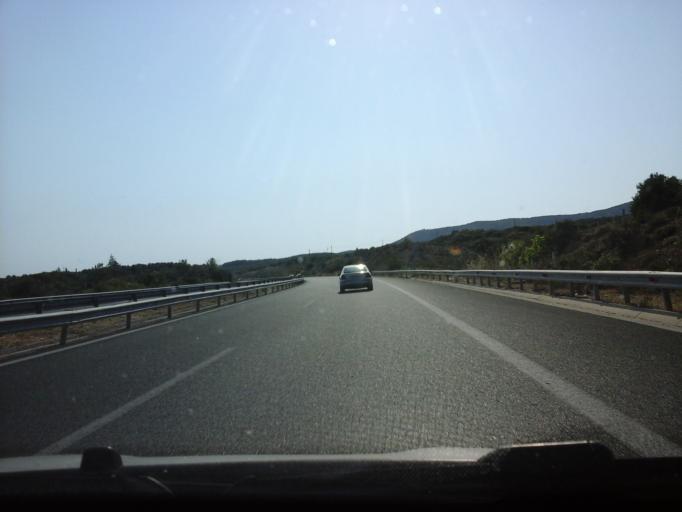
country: GR
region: East Macedonia and Thrace
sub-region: Nomos Evrou
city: Alexandroupoli
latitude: 40.8675
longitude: 25.7731
